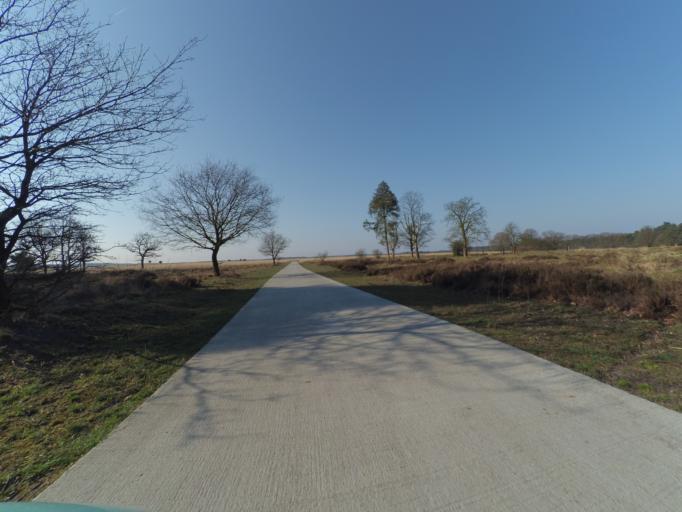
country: NL
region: Gelderland
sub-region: Gemeente Ede
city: Otterlo
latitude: 52.1037
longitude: 5.8718
